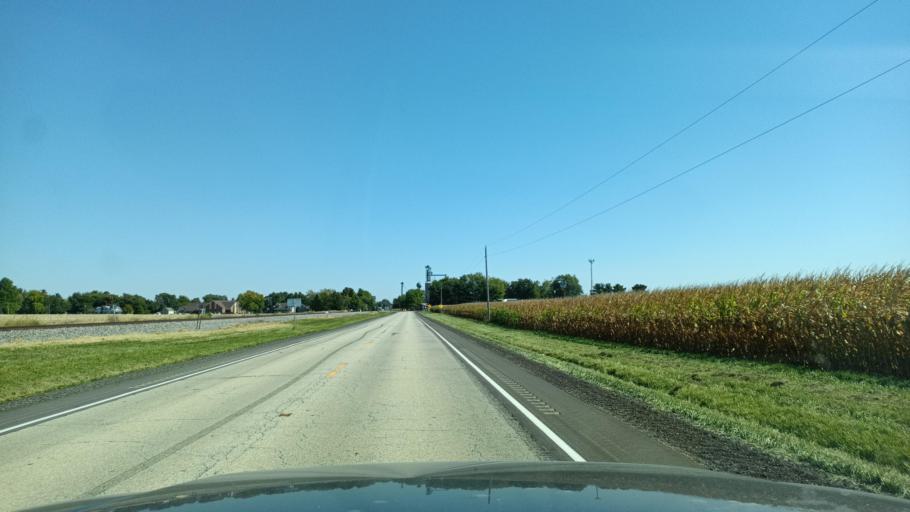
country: US
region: Illinois
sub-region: Woodford County
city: Eureka
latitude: 40.6277
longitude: -89.2877
